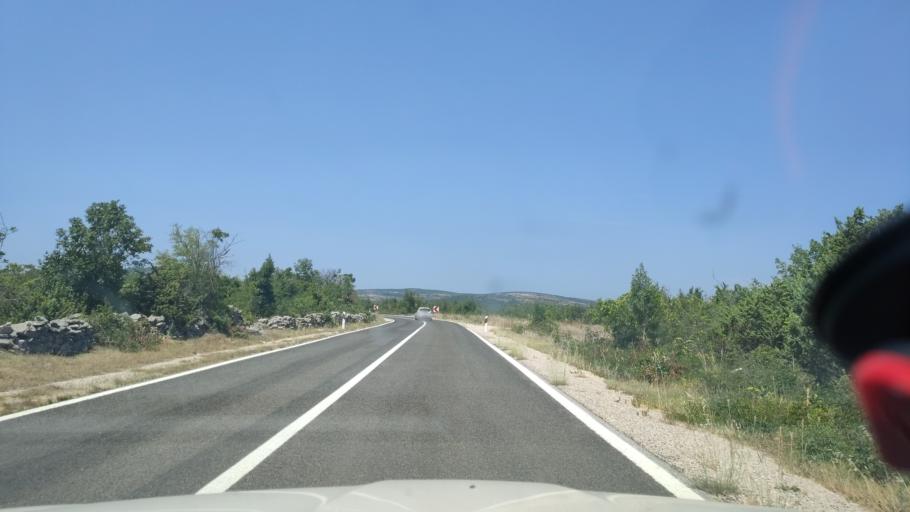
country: HR
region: Sibensko-Kniniska
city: Kistanje
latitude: 43.9722
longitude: 15.8996
